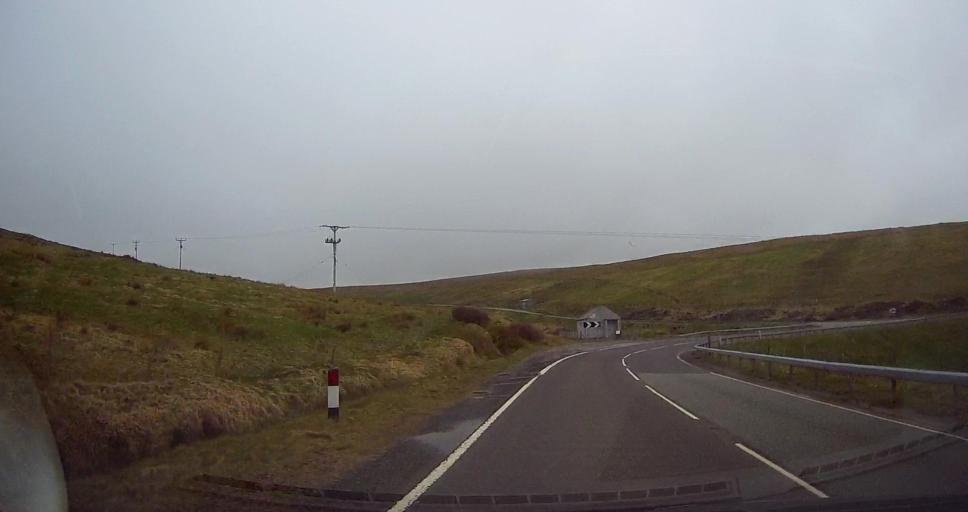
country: GB
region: Scotland
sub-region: Shetland Islands
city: Sandwick
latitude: 59.9864
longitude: -1.2831
